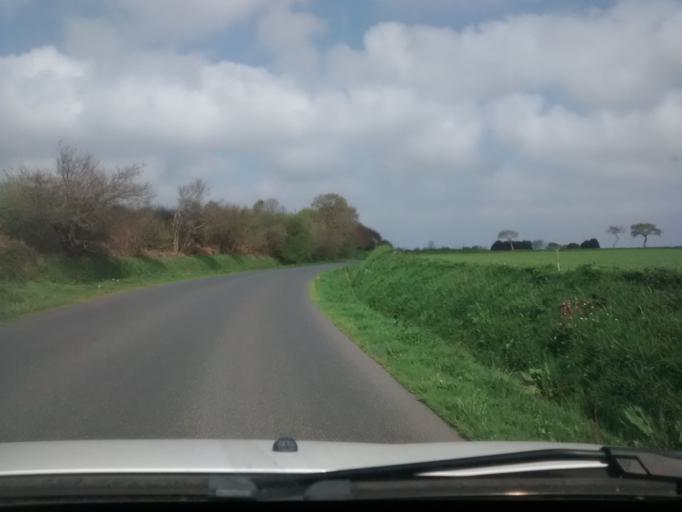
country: FR
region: Brittany
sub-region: Departement des Cotes-d'Armor
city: Trevou-Treguignec
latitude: 48.7948
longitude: -3.3467
